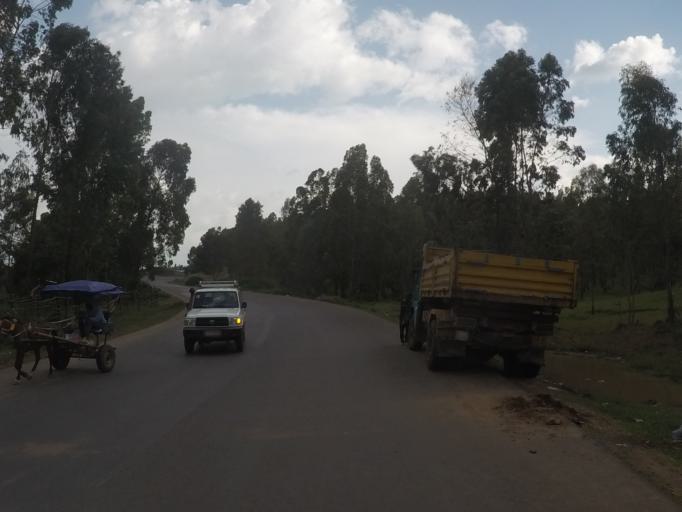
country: ET
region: Amhara
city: Gondar
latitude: 12.6394
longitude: 37.4721
